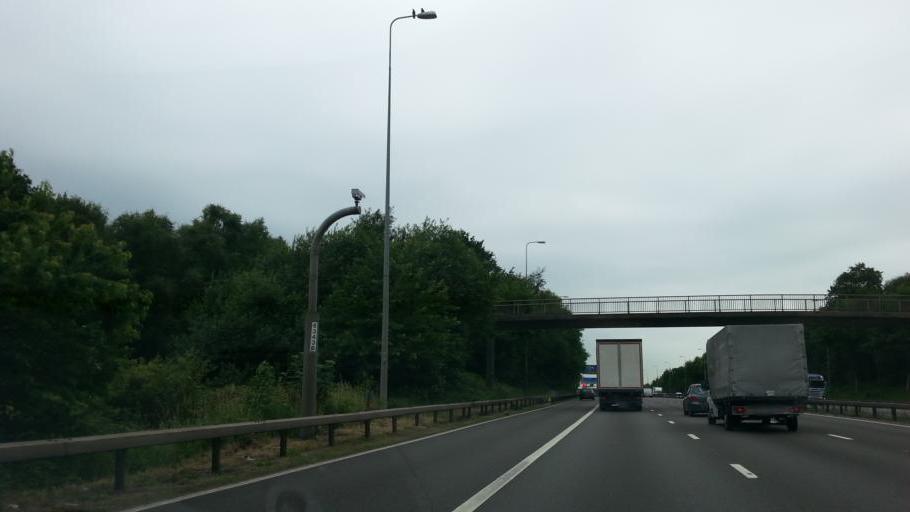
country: GB
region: England
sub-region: Solihull
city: Solihull
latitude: 52.3893
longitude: -1.7758
